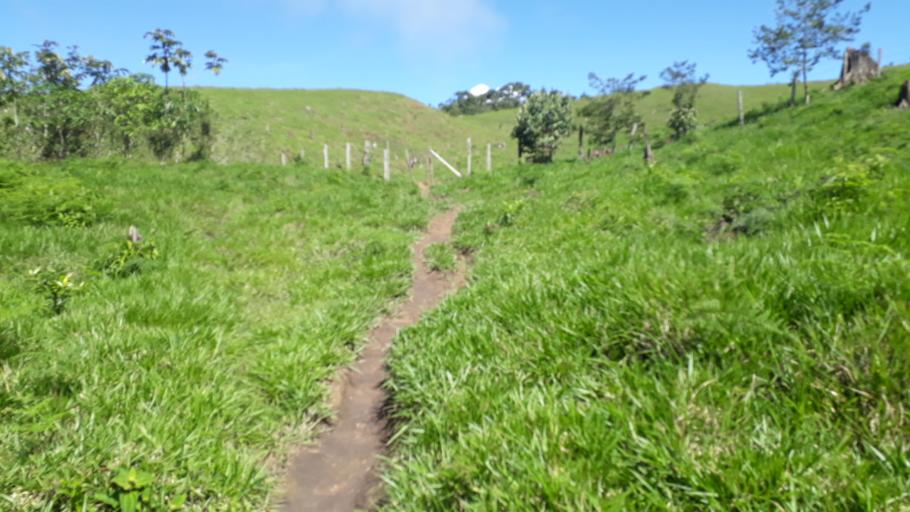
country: CO
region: Casanare
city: Nunchia
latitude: 5.6699
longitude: -72.4328
